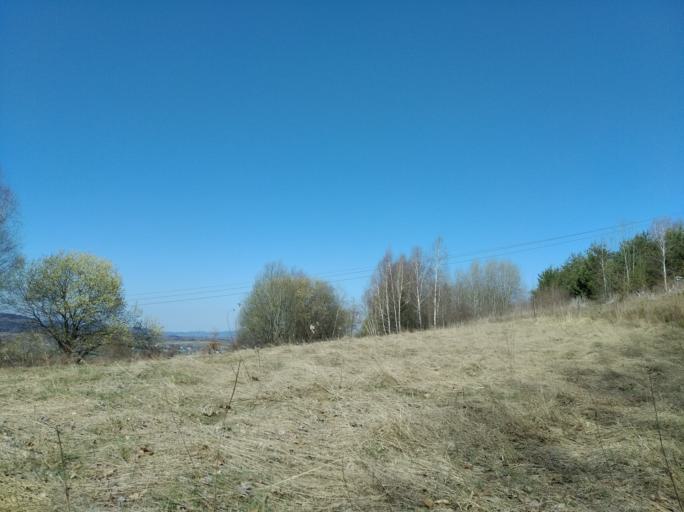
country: PL
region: Subcarpathian Voivodeship
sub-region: Powiat strzyzowski
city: Jawornik
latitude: 49.8356
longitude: 21.8511
